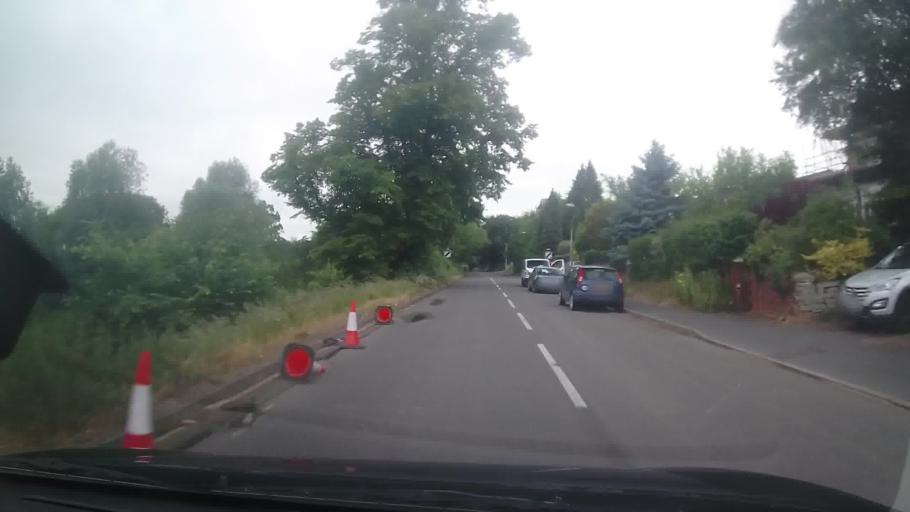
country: GB
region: England
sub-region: Shropshire
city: Shrewsbury
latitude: 52.7195
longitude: -2.7621
